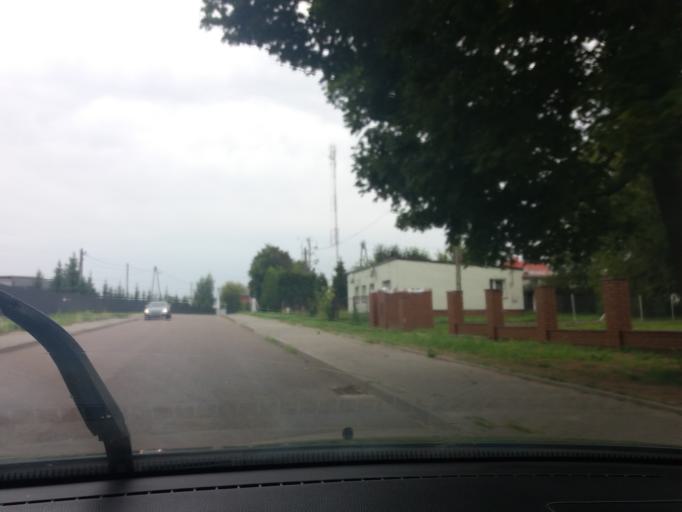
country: PL
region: Masovian Voivodeship
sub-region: Powiat mlawski
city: Wieczfnia Koscielna
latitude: 53.1924
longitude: 20.4686
